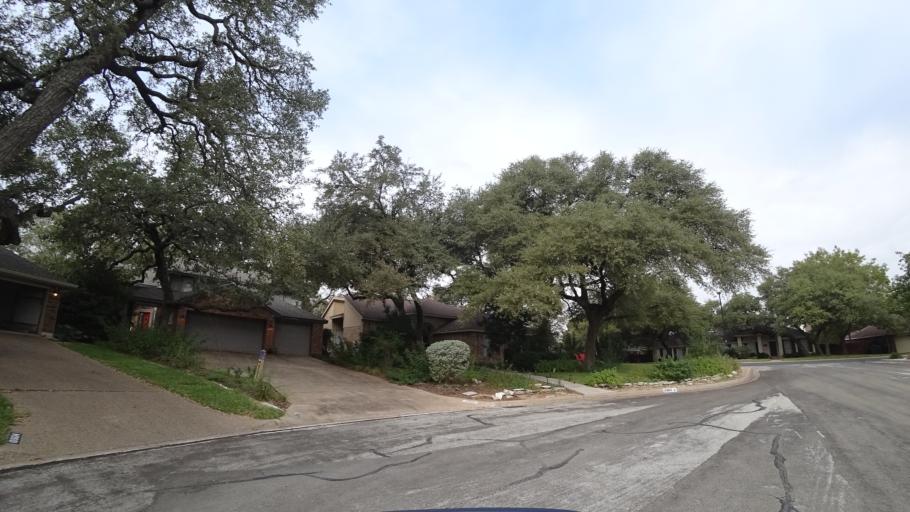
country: US
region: Texas
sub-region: Travis County
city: Shady Hollow
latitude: 30.1899
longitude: -97.8939
